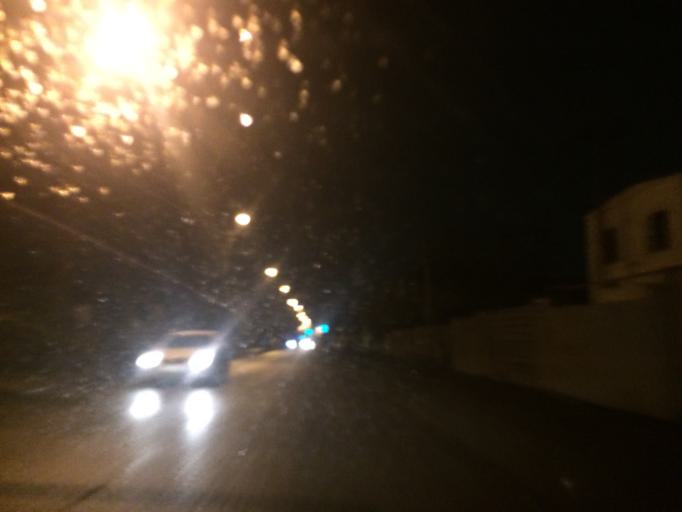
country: KZ
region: Astana Qalasy
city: Astana
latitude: 51.1881
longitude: 71.3842
